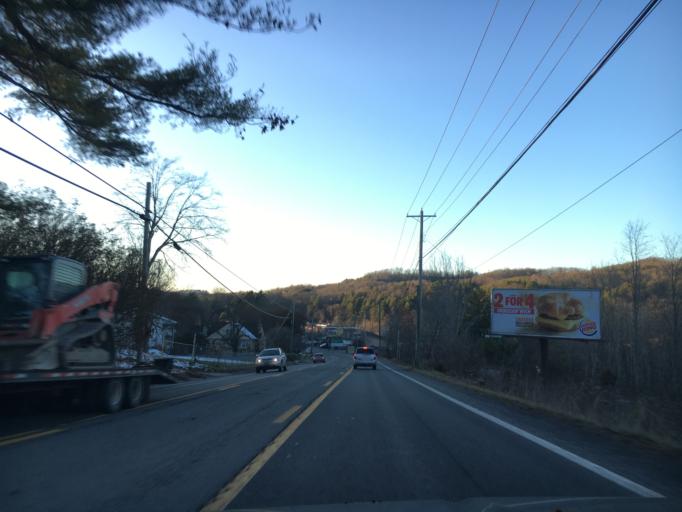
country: US
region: West Virginia
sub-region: Raleigh County
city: Daniels
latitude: 37.7474
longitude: -81.1288
